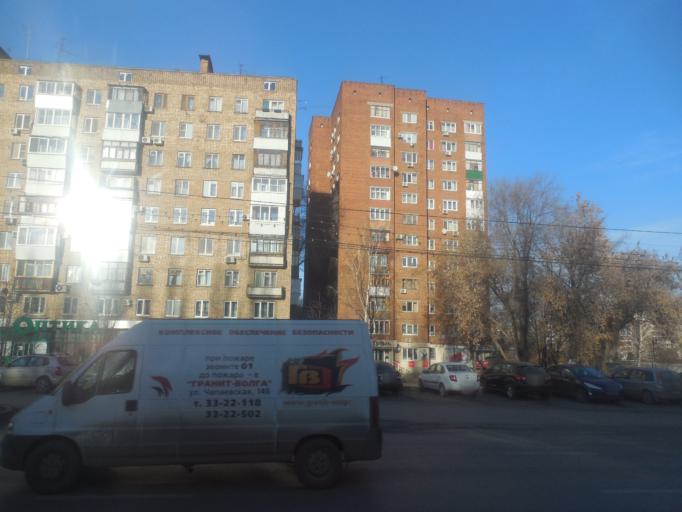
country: RU
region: Samara
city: Samara
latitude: 53.2071
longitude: 50.1343
